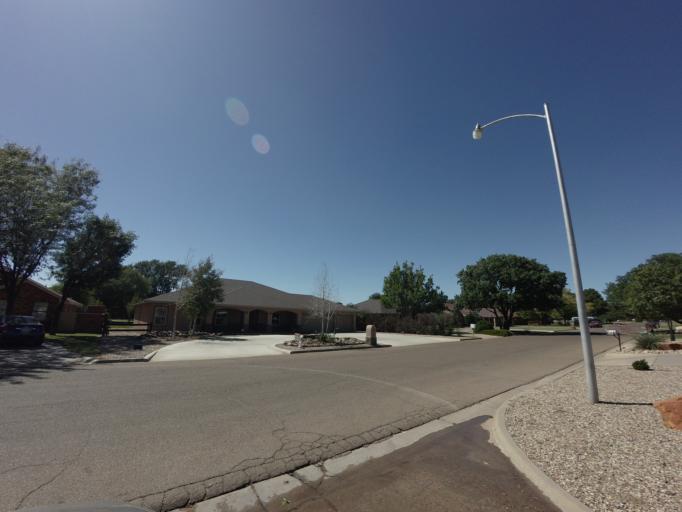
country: US
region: New Mexico
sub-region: Curry County
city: Clovis
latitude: 34.4420
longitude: -103.1890
